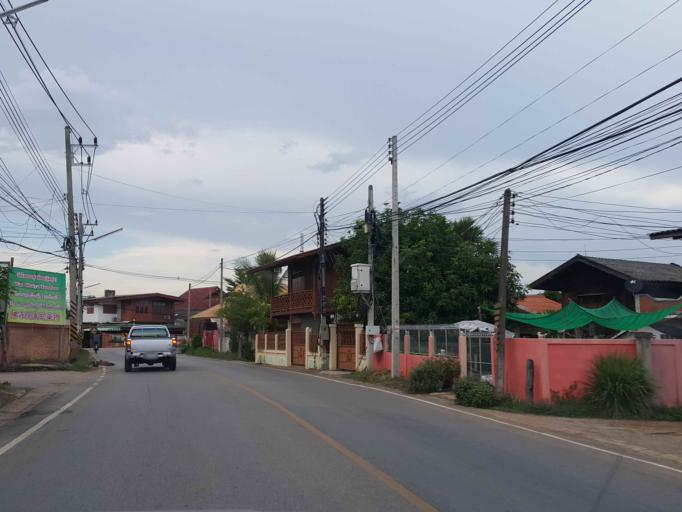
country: TH
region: Lampang
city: Ko Kha
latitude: 18.2639
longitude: 99.3885
